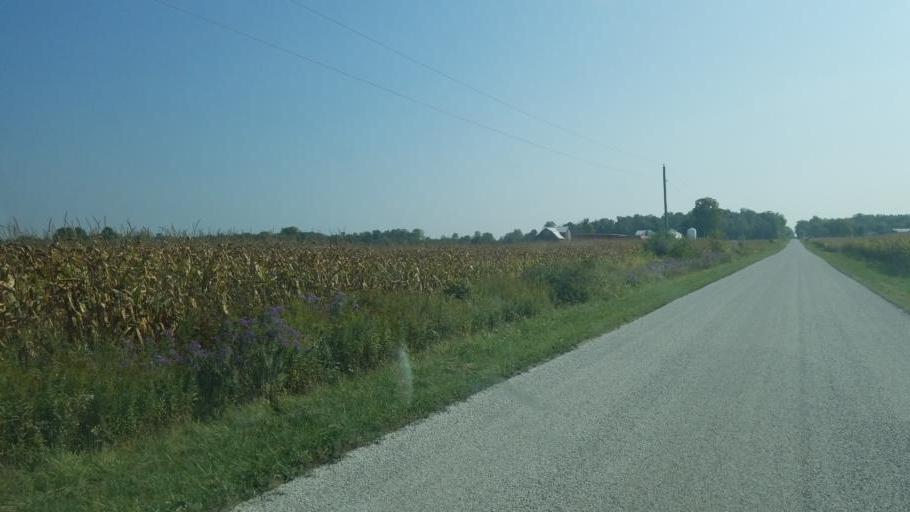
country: US
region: Ohio
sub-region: Crawford County
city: Galion
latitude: 40.6543
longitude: -82.8081
